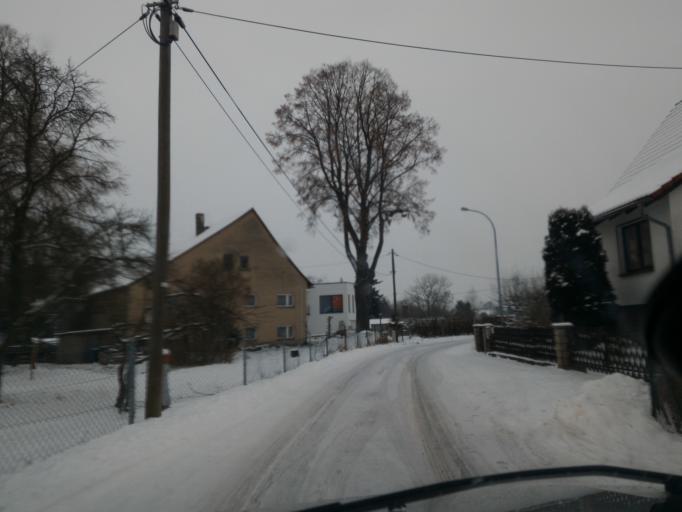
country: DE
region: Saxony
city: Seifhennersdorf
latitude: 50.9374
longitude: 14.5847
